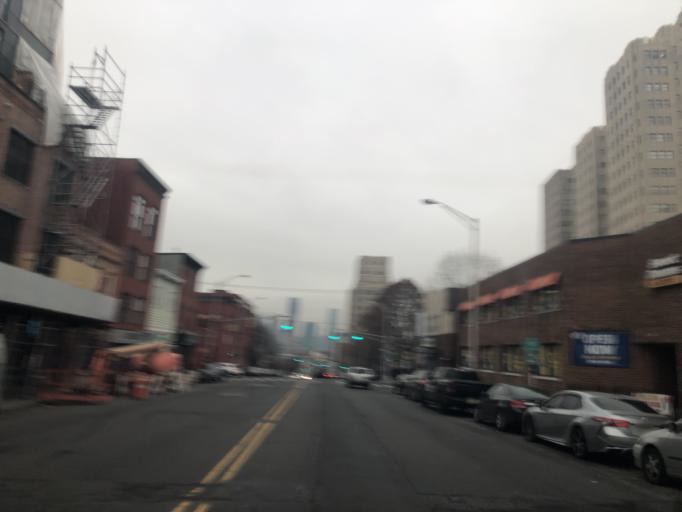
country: US
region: New Jersey
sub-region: Hudson County
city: Jersey City
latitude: 40.7241
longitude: -74.0651
